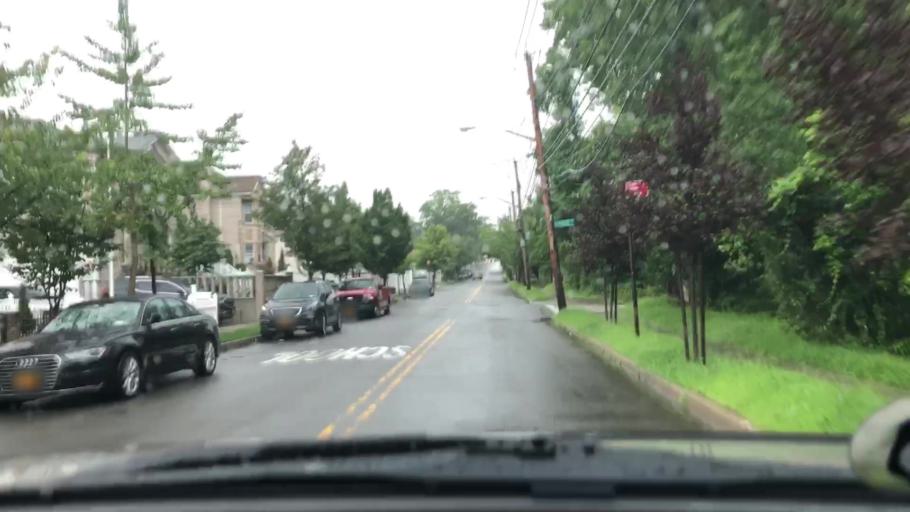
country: US
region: New York
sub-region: Richmond County
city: Staten Island
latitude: 40.5296
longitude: -74.1901
